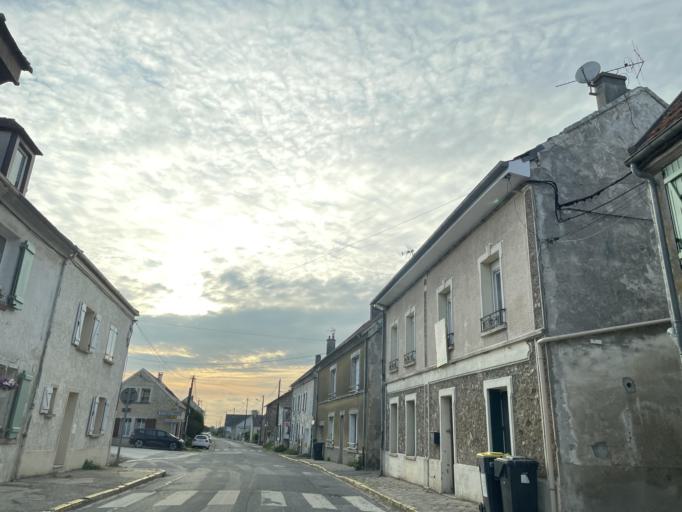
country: FR
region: Ile-de-France
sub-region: Departement de Seine-et-Marne
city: Bouleurs
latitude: 48.8911
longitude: 2.9288
